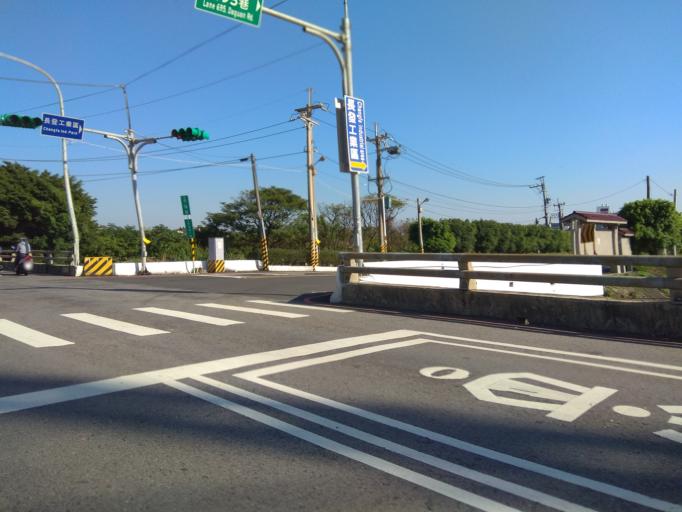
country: TW
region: Taiwan
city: Taoyuan City
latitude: 25.0630
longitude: 121.1778
